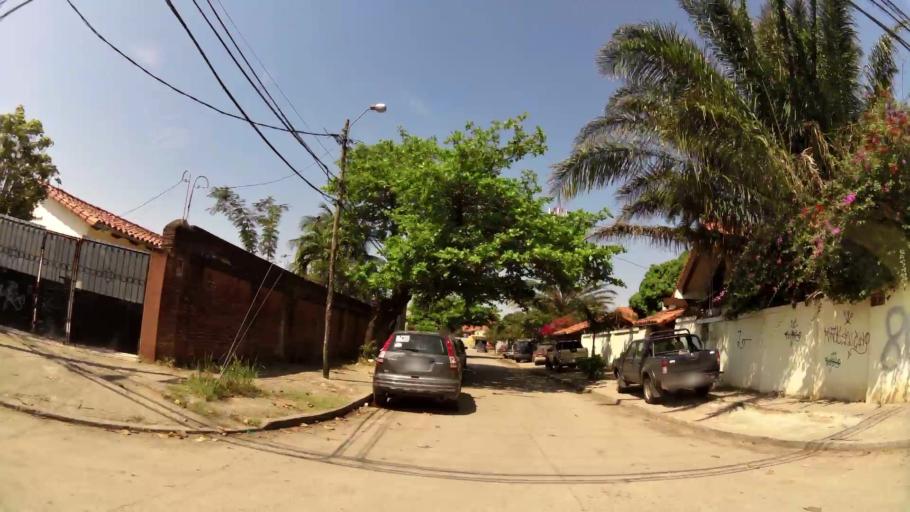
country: BO
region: Santa Cruz
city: Santa Cruz de la Sierra
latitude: -17.7487
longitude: -63.1882
